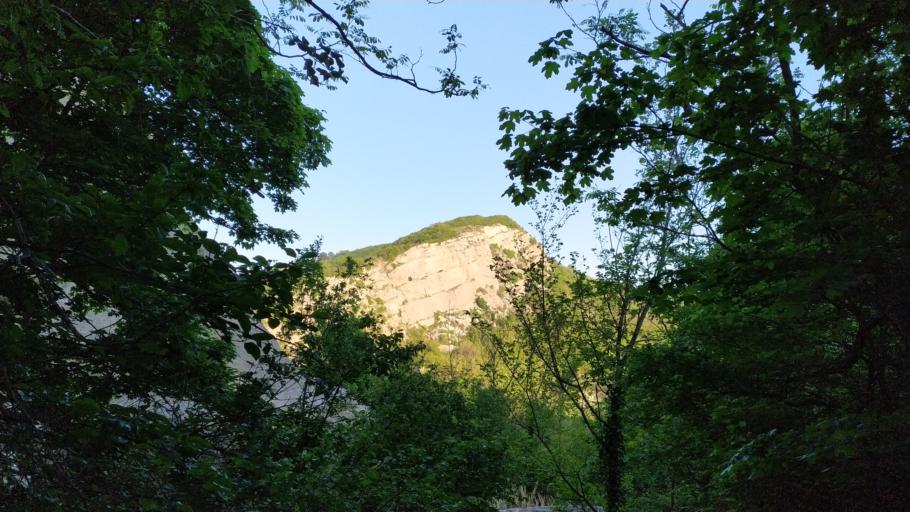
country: IT
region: Emilia-Romagna
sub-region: Provincia di Bologna
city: Borgo Tossignano
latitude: 44.2713
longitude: 11.6070
